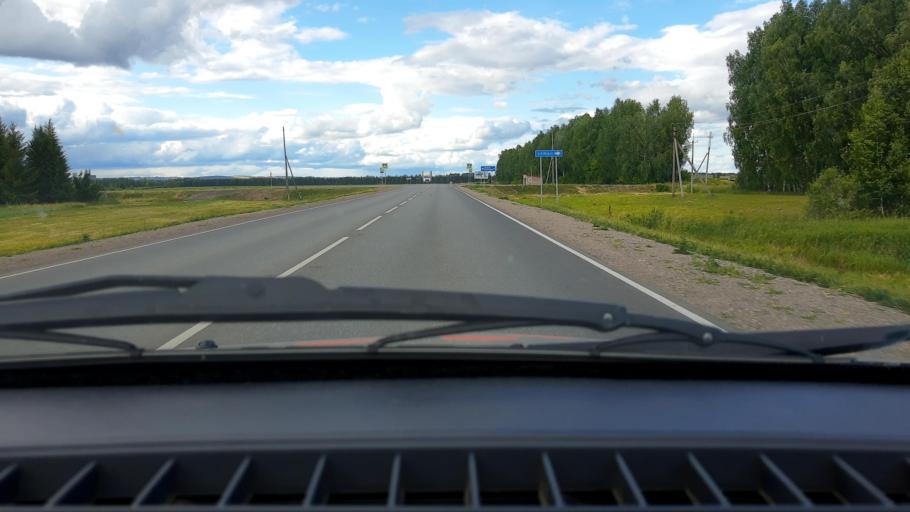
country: RU
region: Bashkortostan
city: Iglino
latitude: 55.0289
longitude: 56.5048
